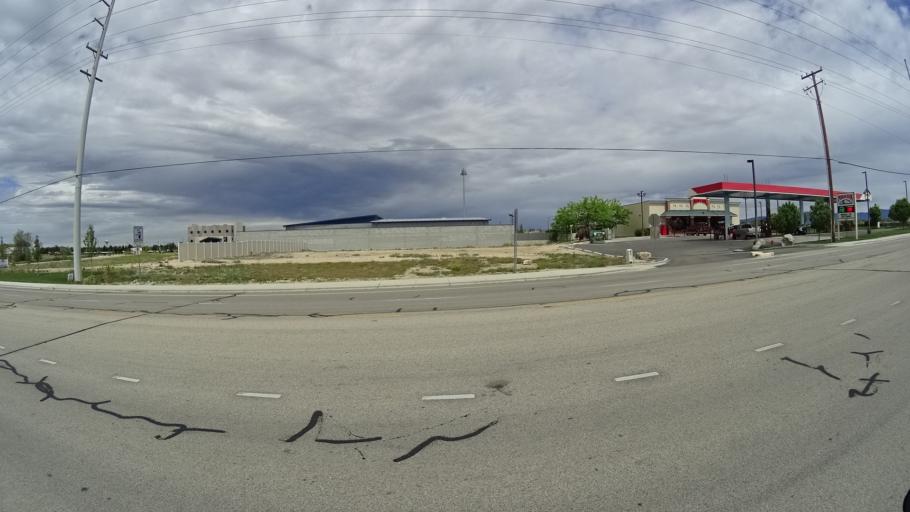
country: US
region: Idaho
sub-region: Ada County
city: Meridian
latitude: 43.5901
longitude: -116.3761
